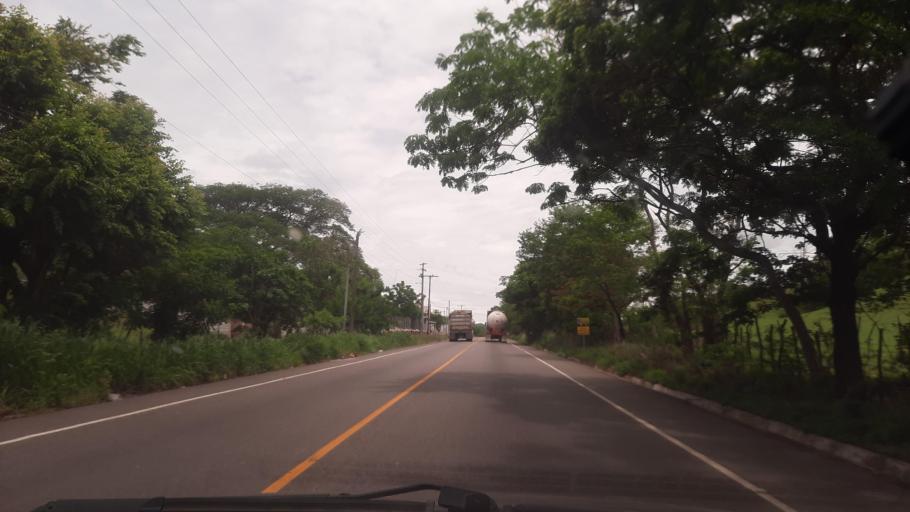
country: GT
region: Zacapa
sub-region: Municipio de Zacapa
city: Gualan
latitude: 15.0878
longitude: -89.4524
